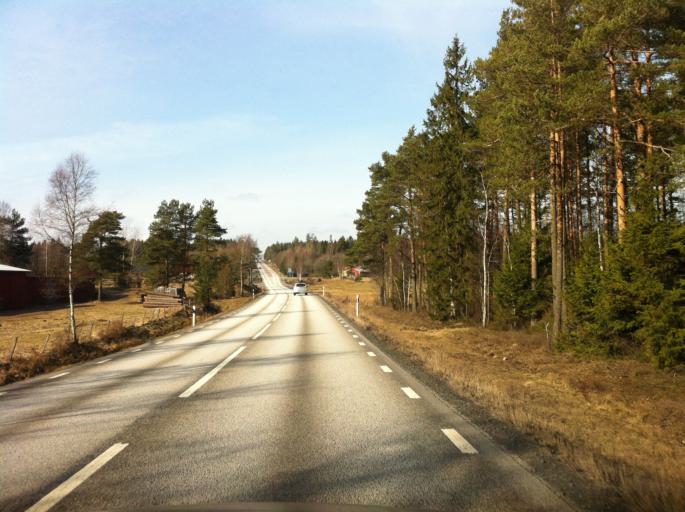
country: SE
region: Joenkoeping
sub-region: Mullsjo Kommun
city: Mullsjoe
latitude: 57.8698
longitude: 13.9508
